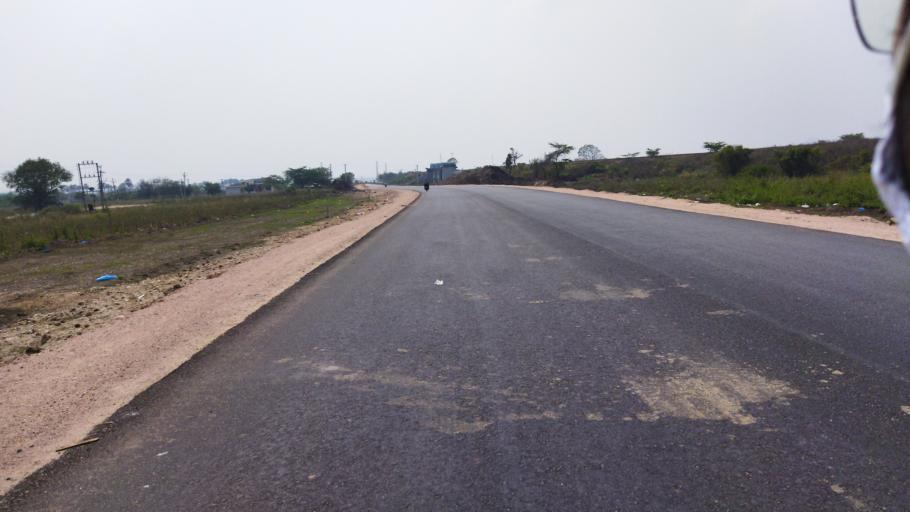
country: IN
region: Telangana
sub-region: Nalgonda
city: Nalgonda
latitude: 17.0769
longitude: 79.3196
